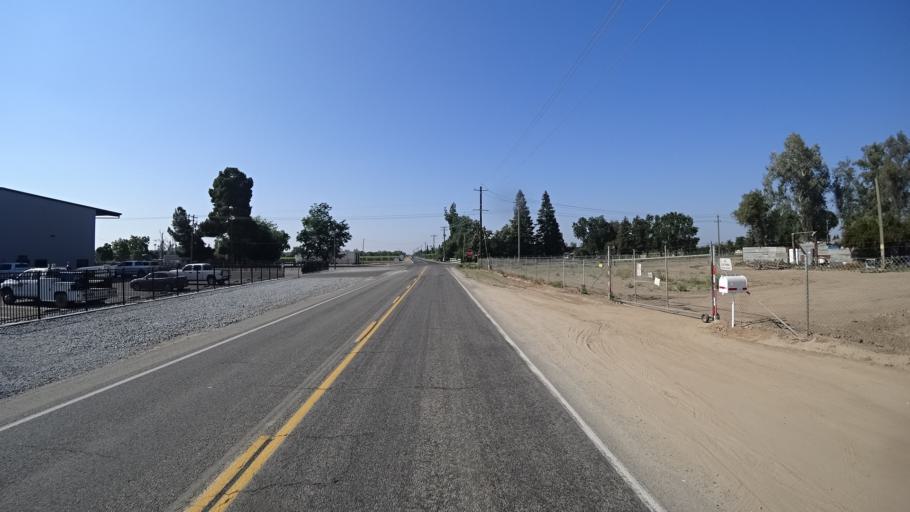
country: US
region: California
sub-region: Fresno County
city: Kingsburg
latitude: 36.4897
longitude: -119.5571
